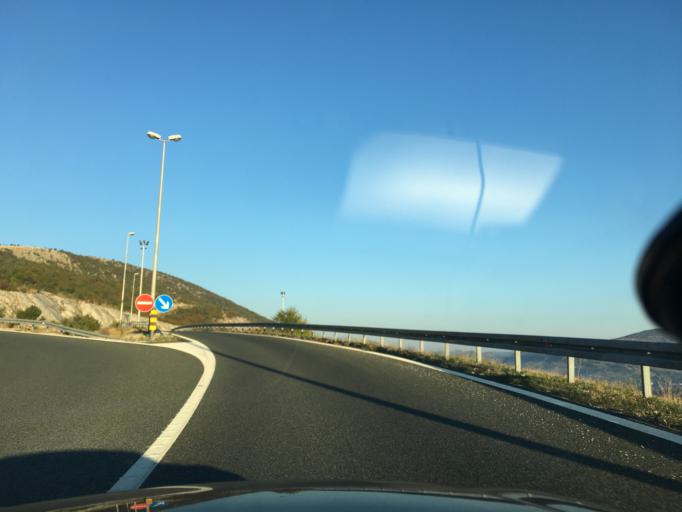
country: HR
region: Splitsko-Dalmatinska
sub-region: Grad Trogir
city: Trogir
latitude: 43.6234
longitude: 16.2423
